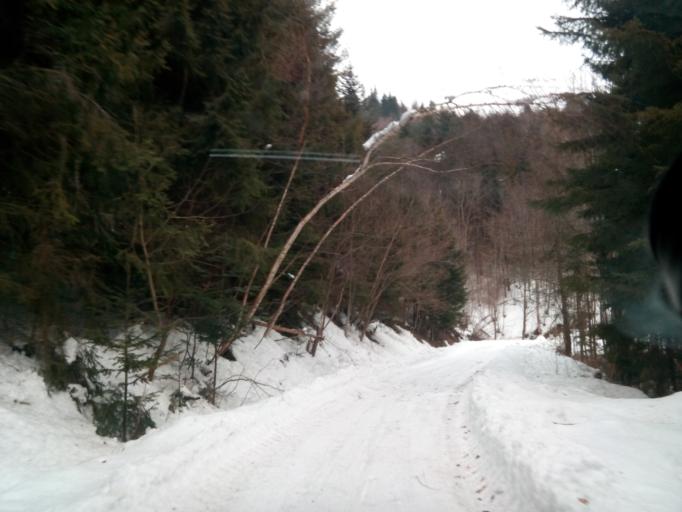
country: SK
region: Presovsky
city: Sabinov
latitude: 49.2151
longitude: 21.0873
